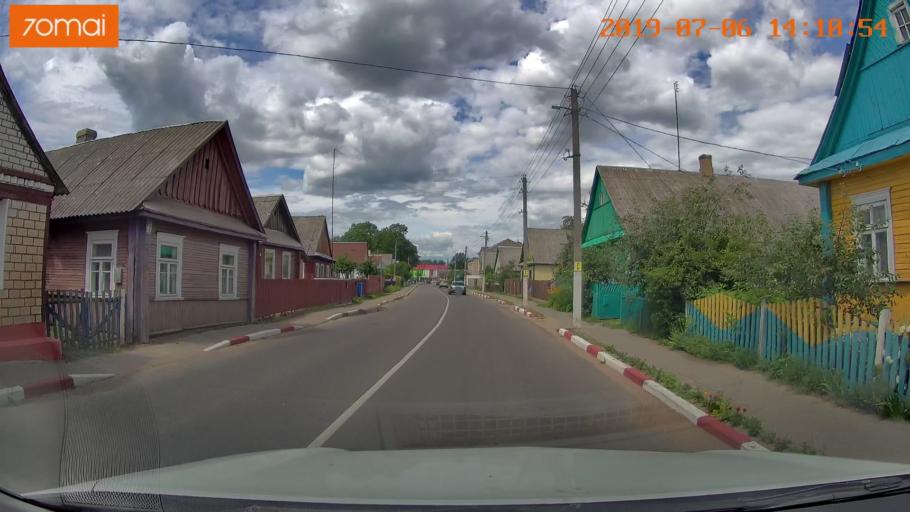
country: BY
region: Minsk
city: Ivyanyets
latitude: 53.8870
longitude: 26.7428
